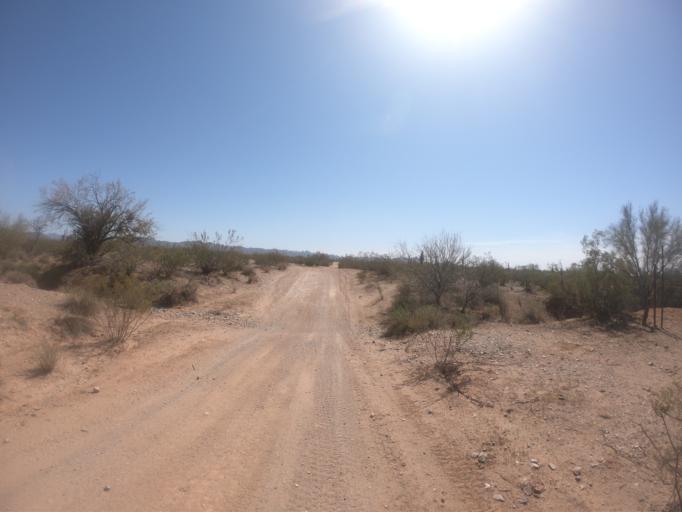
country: US
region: Arizona
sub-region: Pinal County
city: Gold Camp
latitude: 33.2441
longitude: -111.3223
